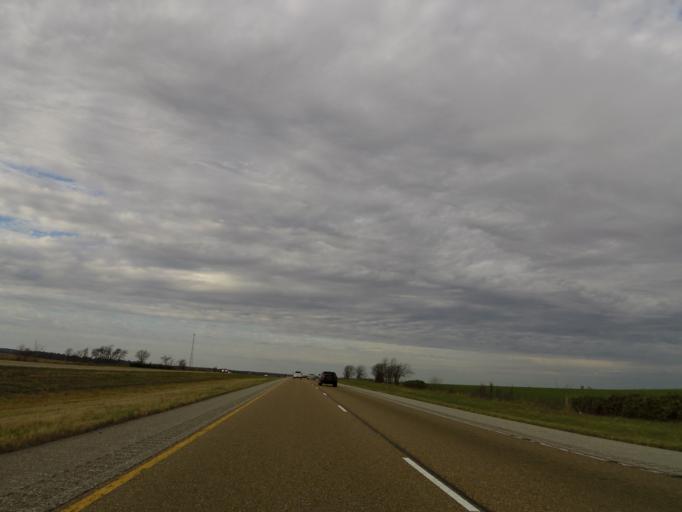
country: US
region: Illinois
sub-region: Washington County
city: Nashville
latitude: 38.3904
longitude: -89.2429
